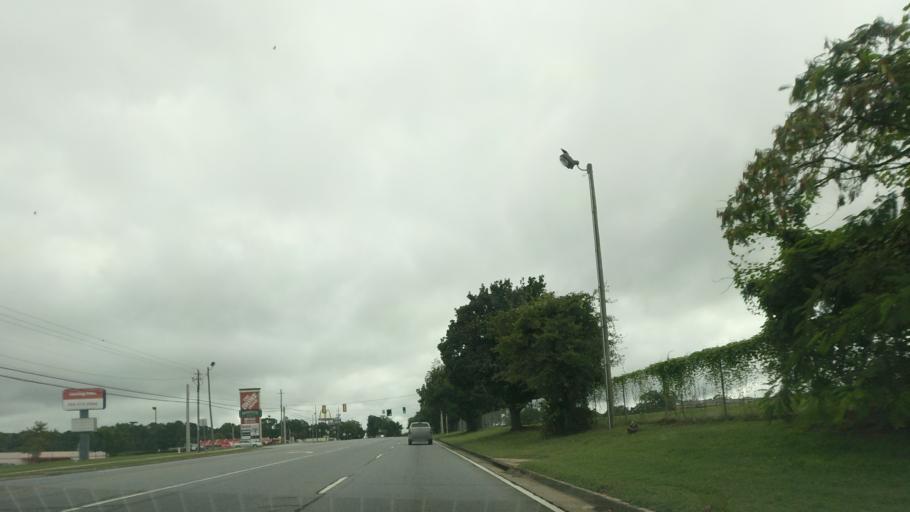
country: US
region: Georgia
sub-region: Laurens County
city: Dublin
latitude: 32.5401
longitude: -82.9453
